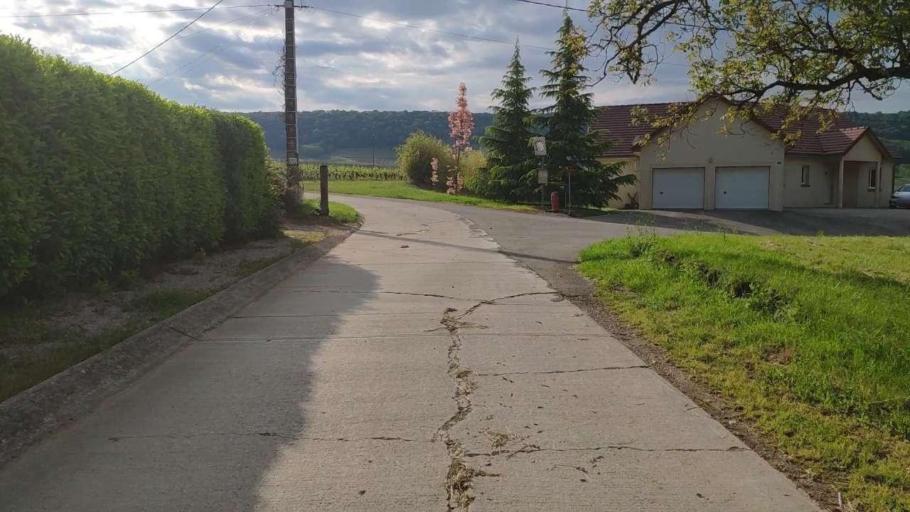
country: FR
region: Franche-Comte
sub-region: Departement du Jura
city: Perrigny
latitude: 46.7335
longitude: 5.5947
